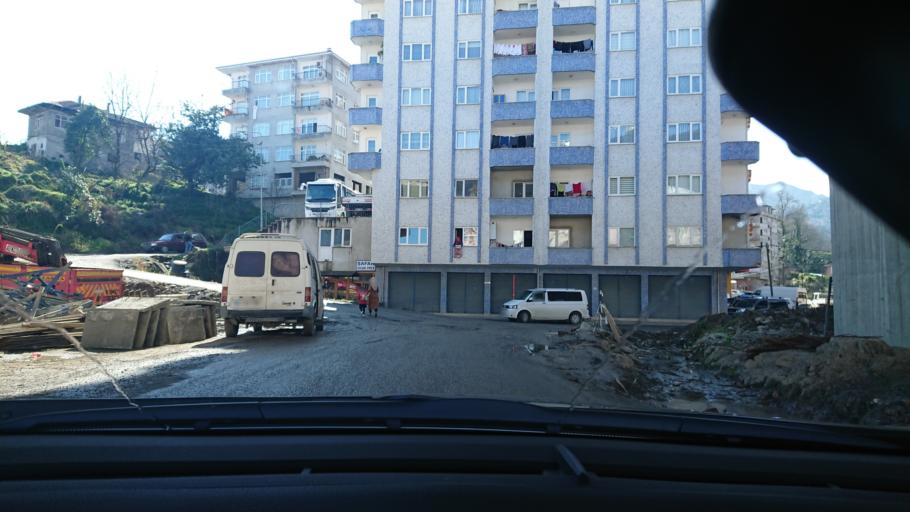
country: TR
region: Rize
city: Rize
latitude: 41.0215
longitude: 40.5260
